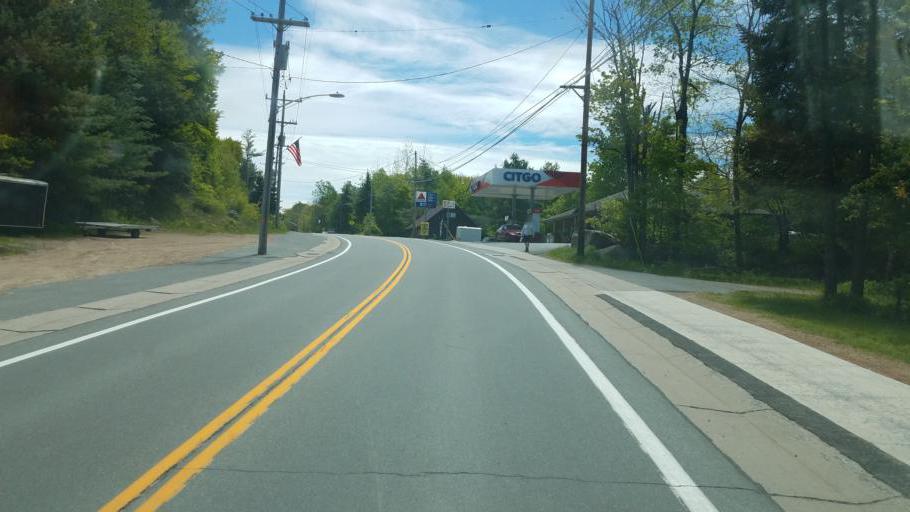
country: US
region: New York
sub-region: Hamilton County
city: Lake Pleasant
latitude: 43.7467
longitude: -74.7883
